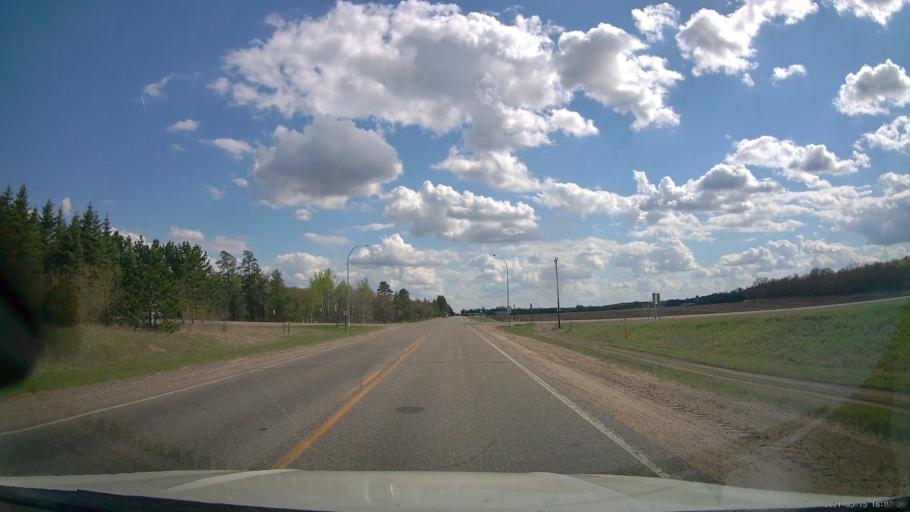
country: US
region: Minnesota
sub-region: Hubbard County
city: Park Rapids
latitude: 46.9653
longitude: -94.9527
